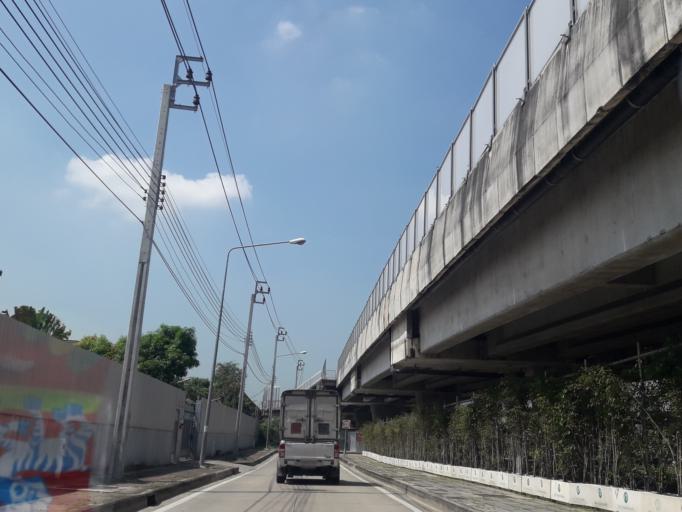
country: TH
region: Bangkok
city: Bangkok Noi
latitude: 13.7542
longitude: 100.4616
